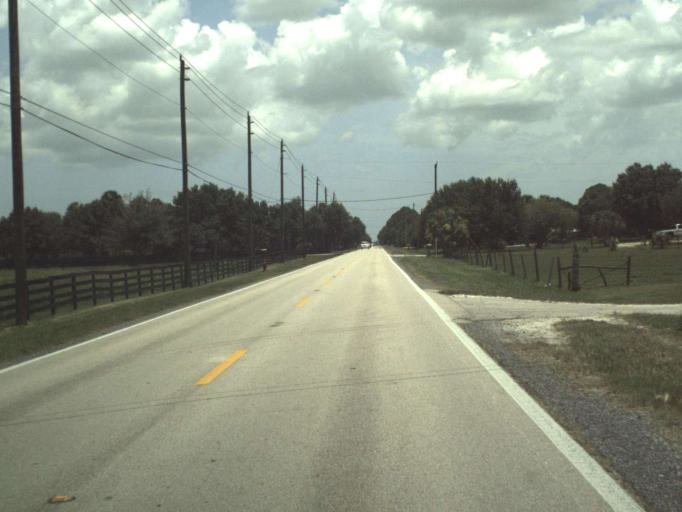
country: US
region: Florida
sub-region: Saint Lucie County
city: Fort Pierce South
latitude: 27.3744
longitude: -80.4372
